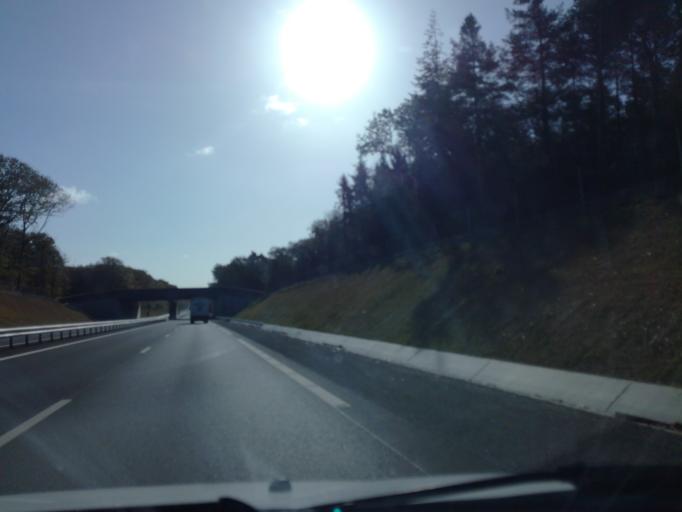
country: FR
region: Brittany
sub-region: Departement d'Ille-et-Vilaine
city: Martigne-Ferchaud
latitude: 47.7911
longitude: -1.2643
